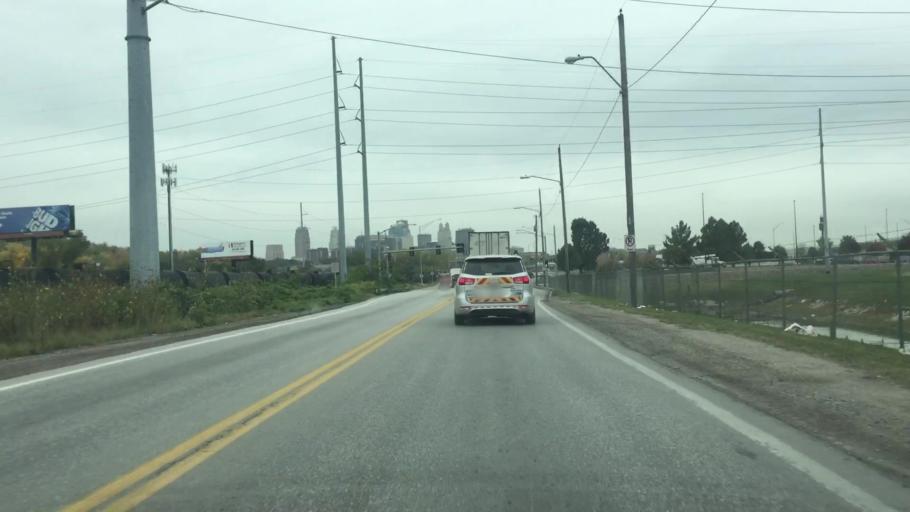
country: US
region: Missouri
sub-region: Clay County
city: North Kansas City
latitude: 39.1212
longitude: -94.5583
